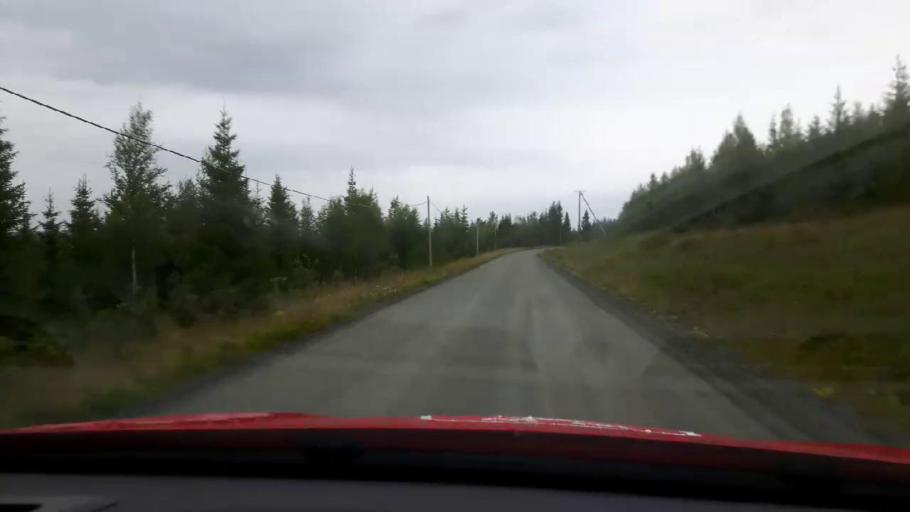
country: SE
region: Jaemtland
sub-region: Are Kommun
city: Are
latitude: 63.4131
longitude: 12.8277
